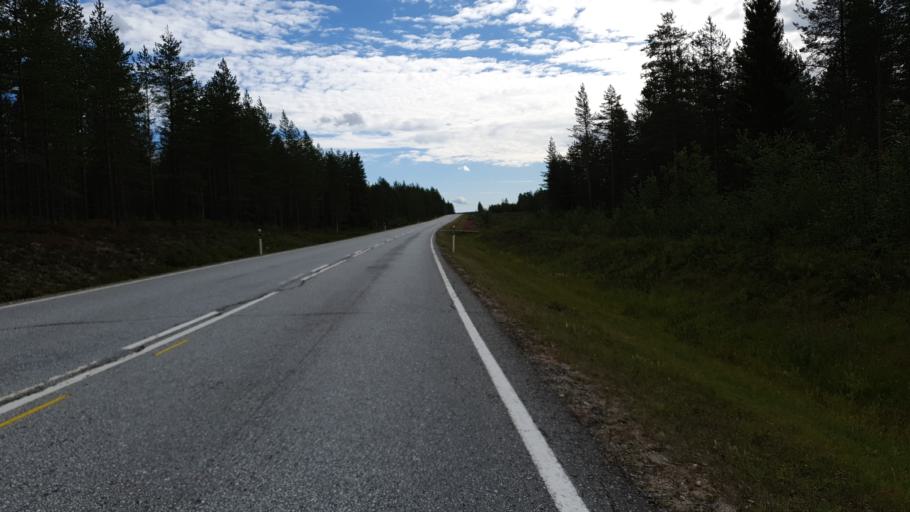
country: FI
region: Kainuu
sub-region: Kehys-Kainuu
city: Kuhmo
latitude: 64.4831
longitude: 29.7827
